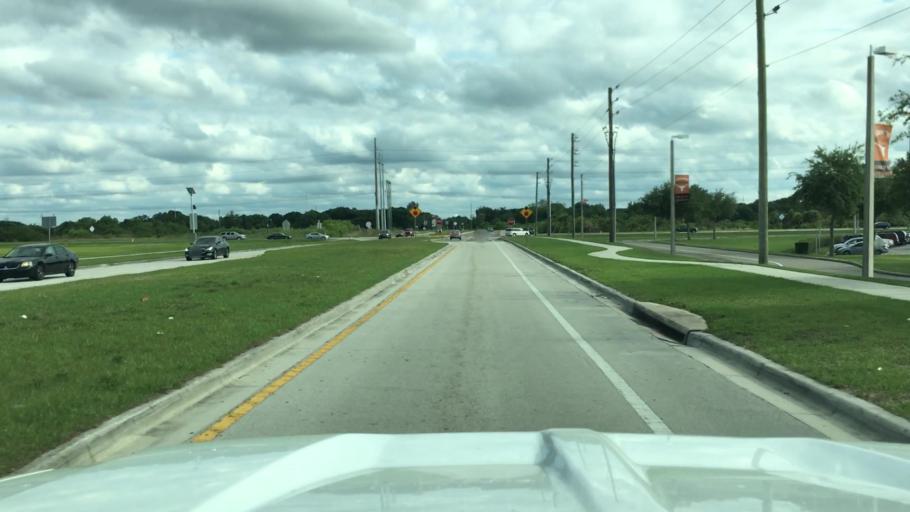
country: US
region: Florida
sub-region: Hillsborough County
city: Ruskin
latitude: 27.7221
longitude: -82.4024
